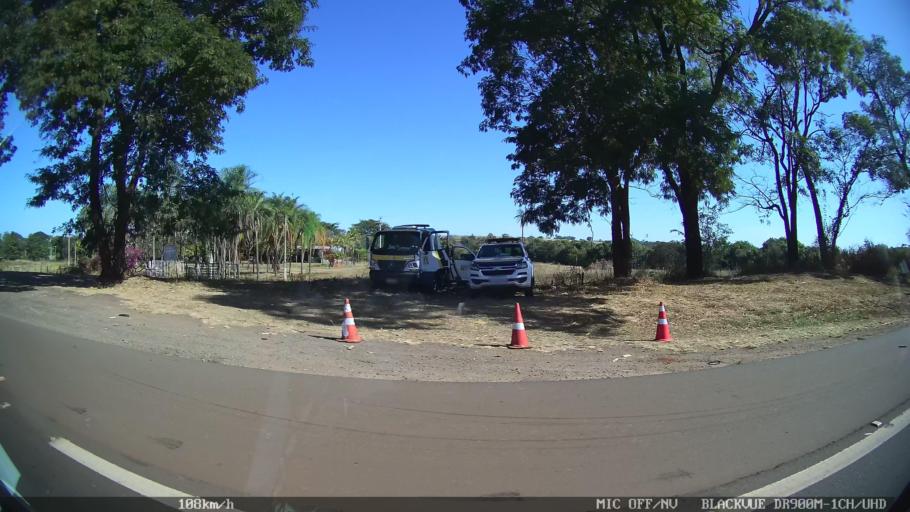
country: BR
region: Sao Paulo
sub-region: Olimpia
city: Olimpia
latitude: -20.6941
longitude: -48.8956
